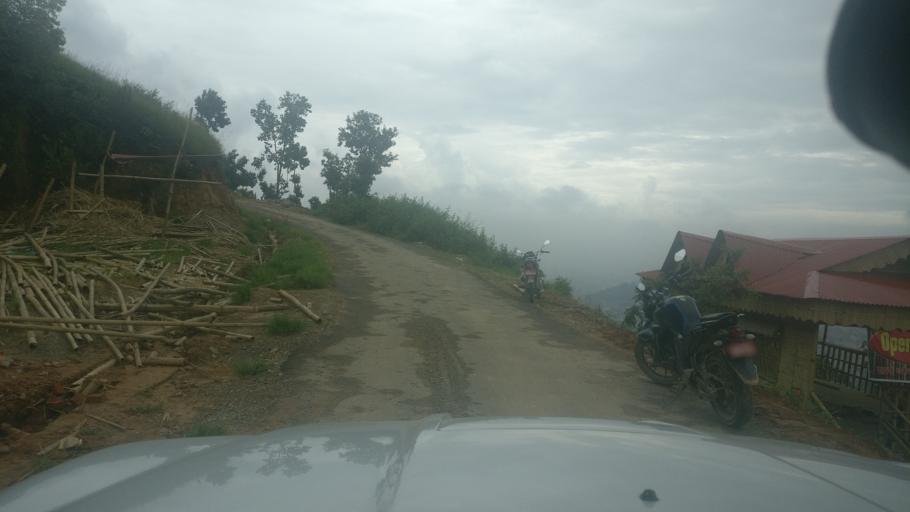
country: NP
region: Central Region
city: Kirtipur
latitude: 27.7042
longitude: 85.2558
